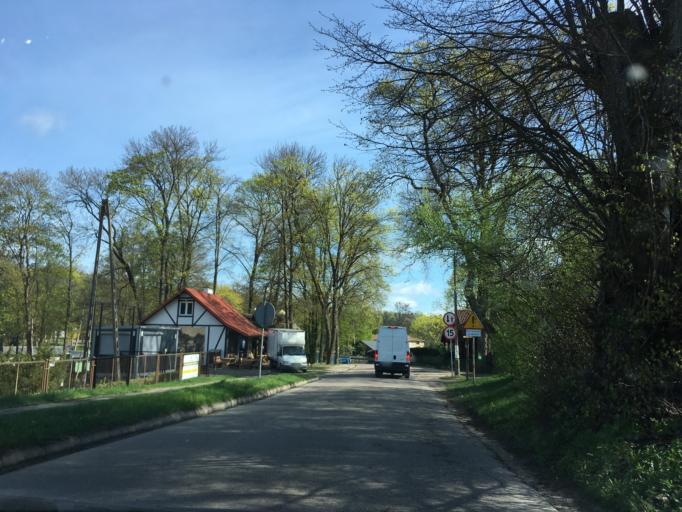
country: PL
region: Warmian-Masurian Voivodeship
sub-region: Powiat piski
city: Ruciane-Nida
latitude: 53.6611
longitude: 21.5675
